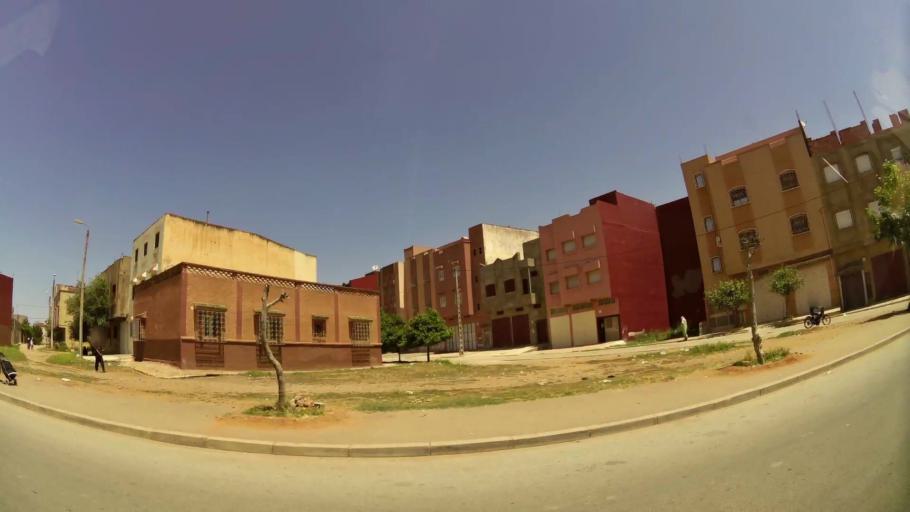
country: MA
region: Rabat-Sale-Zemmour-Zaer
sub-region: Khemisset
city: Khemisset
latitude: 33.8343
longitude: -6.0720
